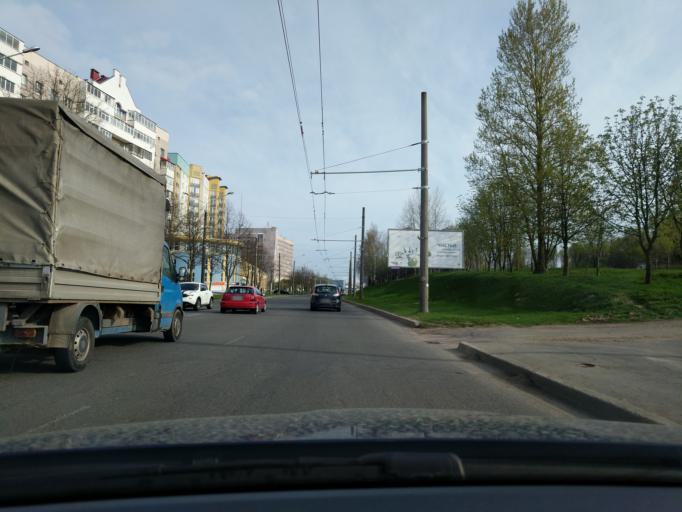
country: BY
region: Minsk
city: Novoye Medvezhino
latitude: 53.9045
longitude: 27.4629
